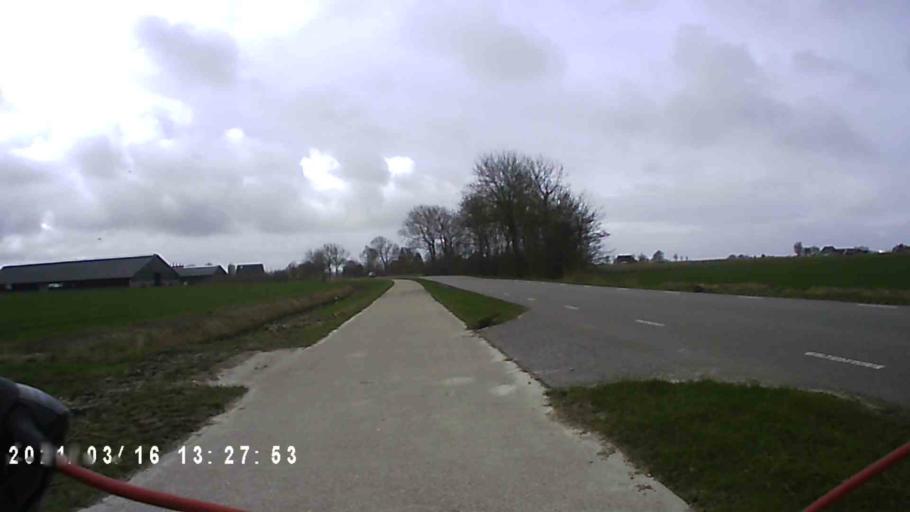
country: NL
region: Friesland
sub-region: Gemeente Franekeradeel
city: Tzummarum
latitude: 53.2171
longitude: 5.5715
